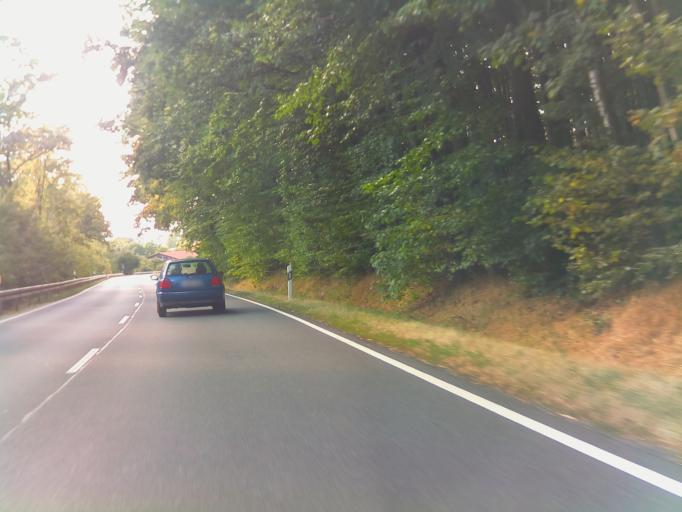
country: DE
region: Hesse
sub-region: Regierungsbezirk Kassel
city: Poppenhausen
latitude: 50.5249
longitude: 9.8457
